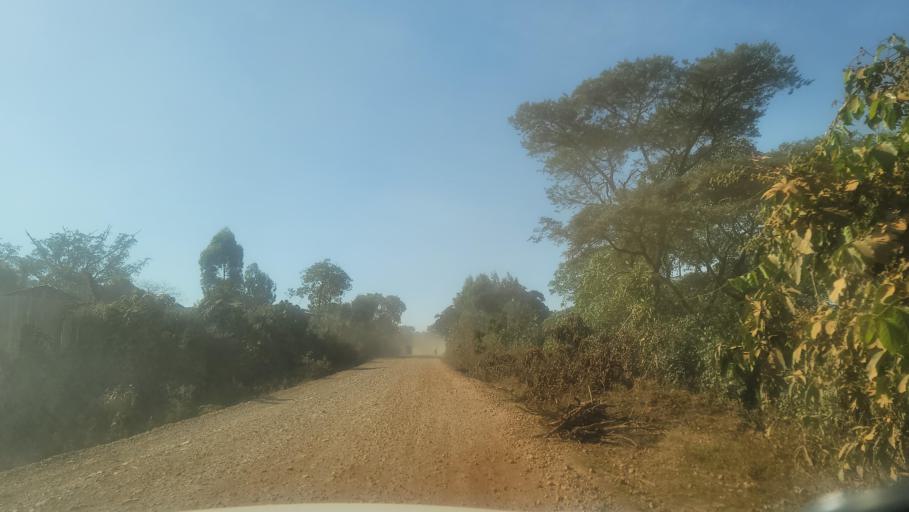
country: ET
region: Oromiya
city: Agaro
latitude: 7.8527
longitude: 36.5675
